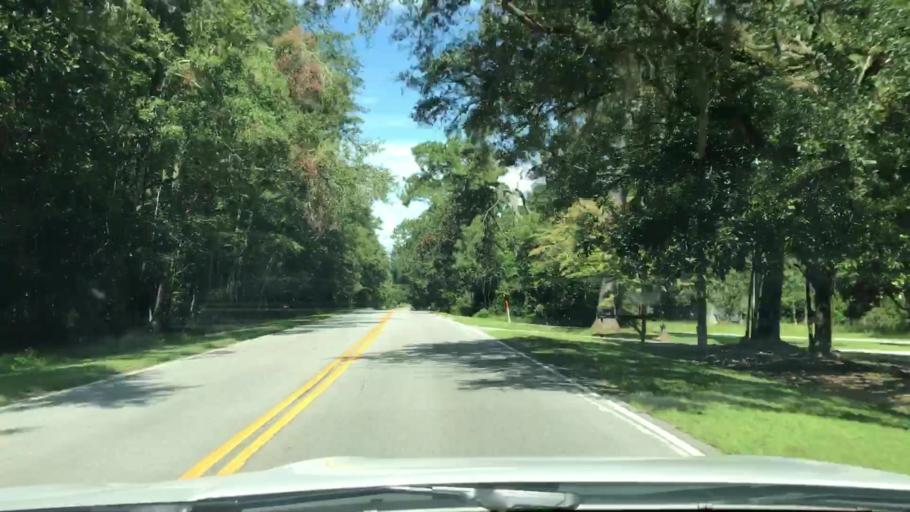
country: US
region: South Carolina
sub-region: Dorchester County
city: Centerville
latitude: 32.9454
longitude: -80.1962
